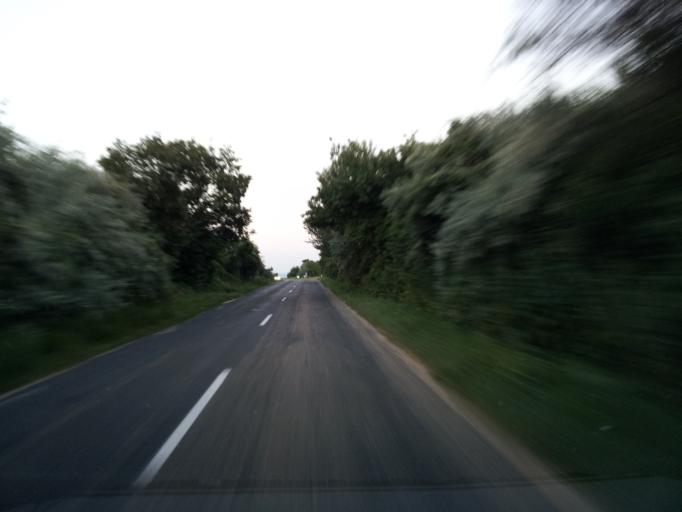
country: HU
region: Fejer
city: Bicske
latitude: 47.4912
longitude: 18.5811
